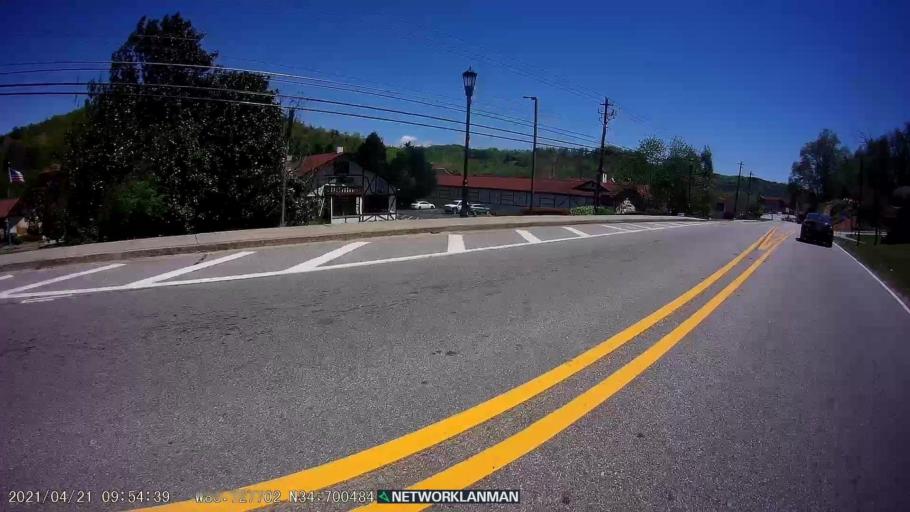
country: US
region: Georgia
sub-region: White County
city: Cleveland
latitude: 34.7004
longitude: -83.7276
